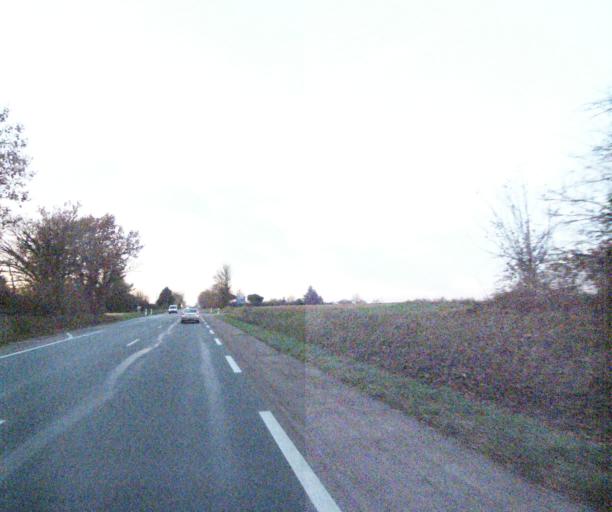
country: FR
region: Poitou-Charentes
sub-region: Departement de la Charente-Maritime
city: Saint-Porchaire
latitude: 45.8071
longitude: -0.7572
